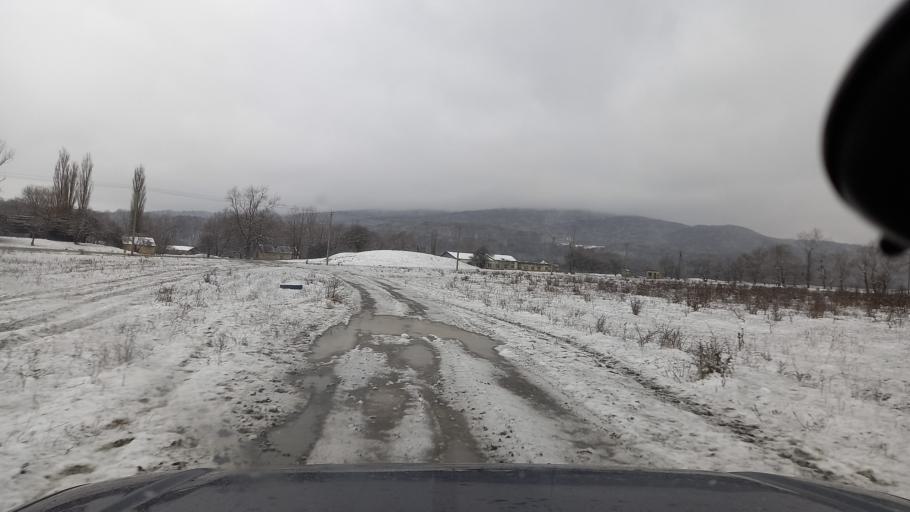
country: RU
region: Adygeya
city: Kamennomostskiy
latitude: 44.2236
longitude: 40.1821
